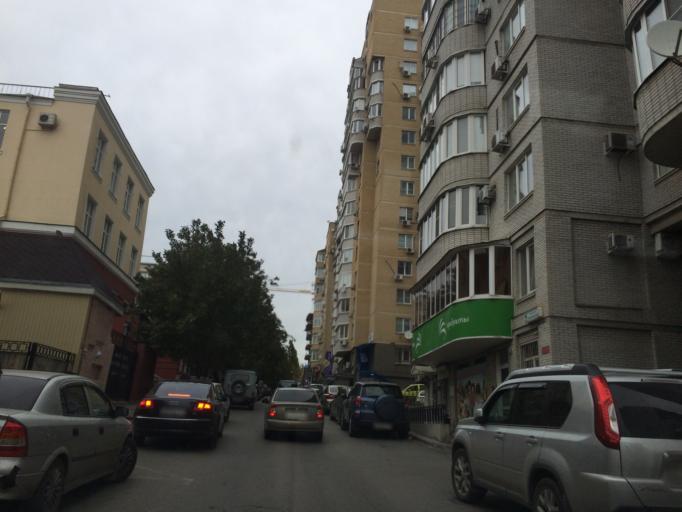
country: RU
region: Rostov
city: Rostov-na-Donu
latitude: 47.2203
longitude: 39.6993
